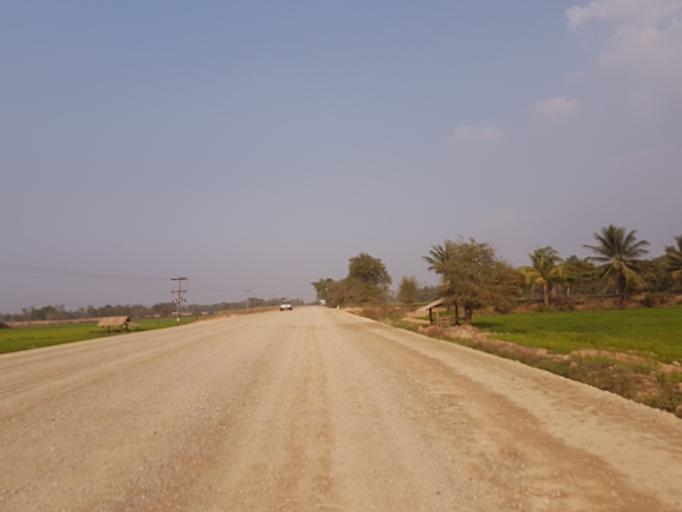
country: TH
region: Nong Khai
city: Phon Phisai
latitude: 17.9912
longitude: 102.9057
